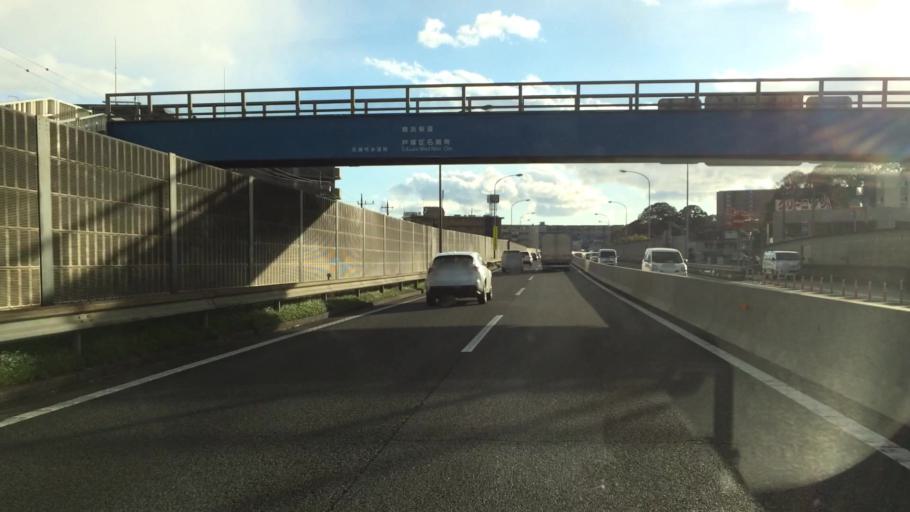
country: JP
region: Kanagawa
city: Fujisawa
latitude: 35.4199
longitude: 139.5381
